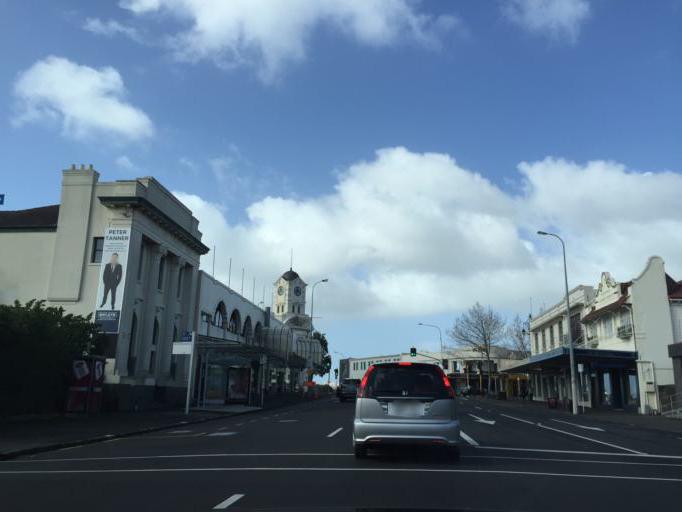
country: NZ
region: Auckland
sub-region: Auckland
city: Auckland
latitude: -36.8469
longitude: 174.7434
